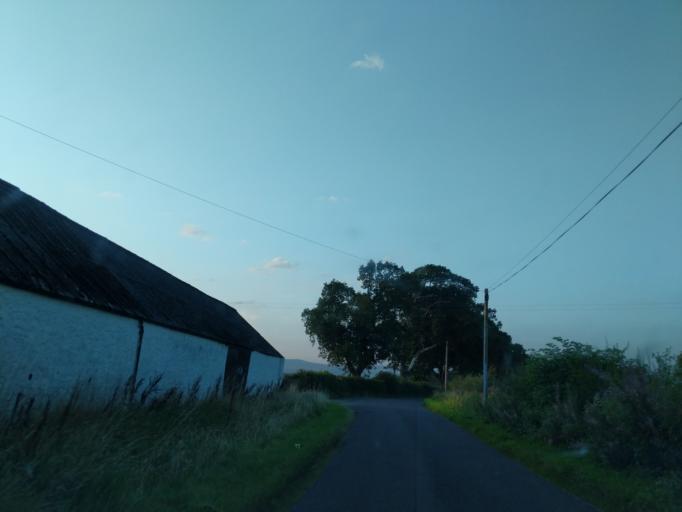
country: GB
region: Scotland
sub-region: Stirling
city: Doune
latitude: 56.1257
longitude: -4.0580
